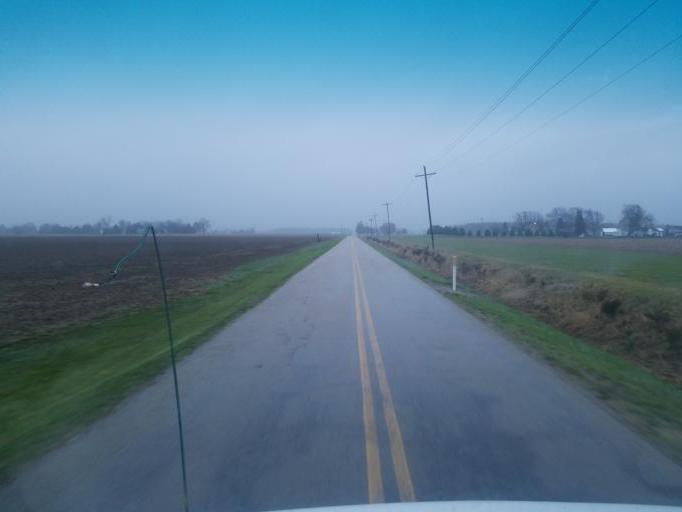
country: US
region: Ohio
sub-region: Fulton County
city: Archbold
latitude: 41.4278
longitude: -84.2520
